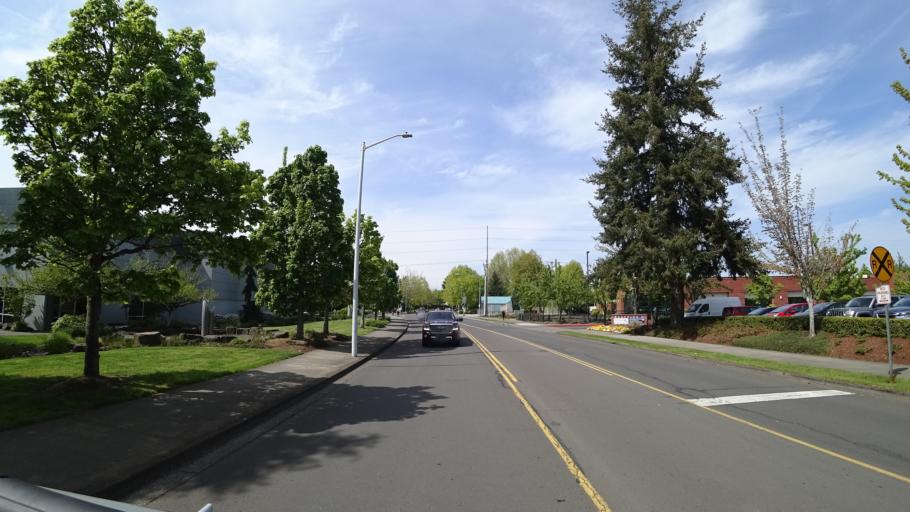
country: US
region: Oregon
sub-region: Washington County
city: Rockcreek
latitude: 45.5292
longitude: -122.9310
